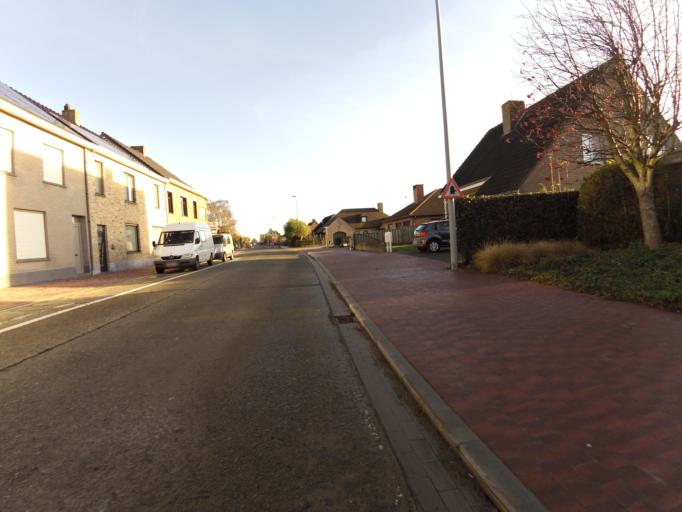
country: BE
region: Flanders
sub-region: Provincie West-Vlaanderen
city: Oudenburg
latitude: 51.1957
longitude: 2.9813
